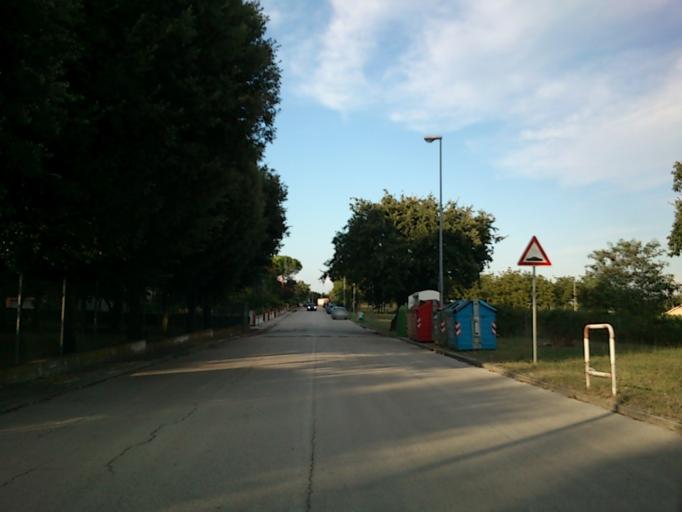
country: IT
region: The Marches
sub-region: Provincia di Pesaro e Urbino
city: Calcinelli
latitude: 43.7517
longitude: 12.9238
